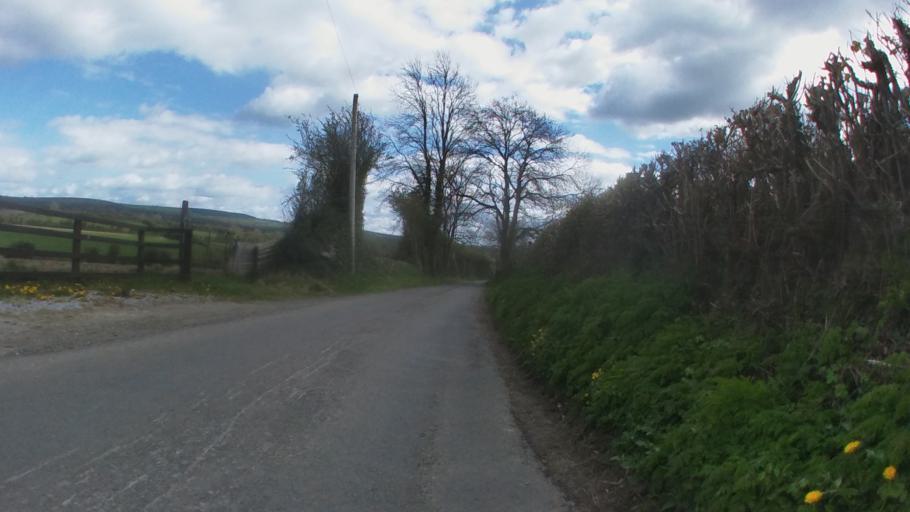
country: IE
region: Leinster
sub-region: Kilkenny
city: Kilkenny
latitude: 52.7022
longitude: -7.2052
